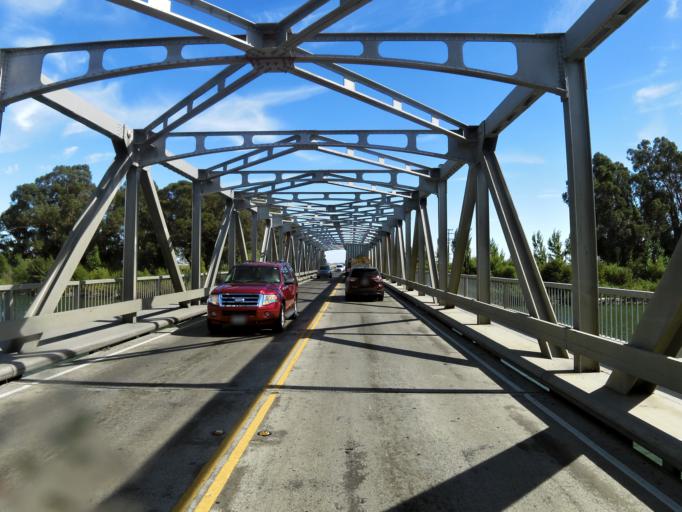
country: US
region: California
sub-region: Solano County
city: Rio Vista
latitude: 38.1573
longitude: -121.6800
